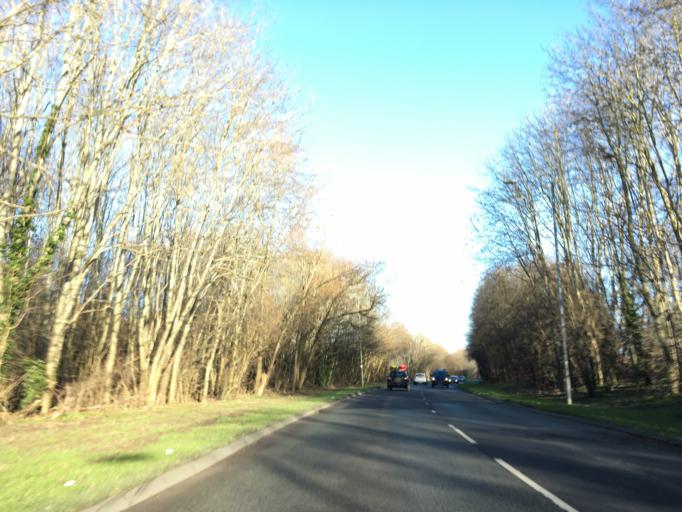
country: GB
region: England
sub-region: Wiltshire
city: Lydiard Tregoze
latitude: 51.5512
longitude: -1.8433
